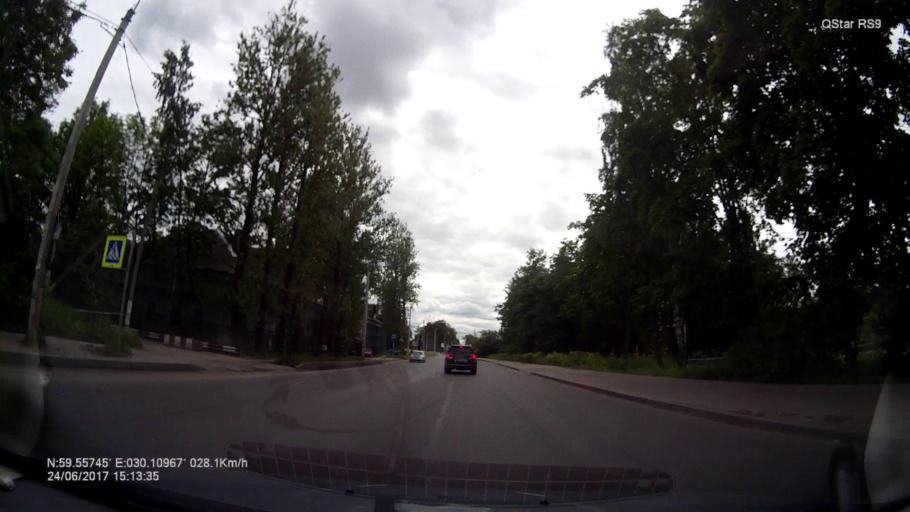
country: RU
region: Leningrad
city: Gatchina
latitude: 59.5574
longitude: 30.1096
